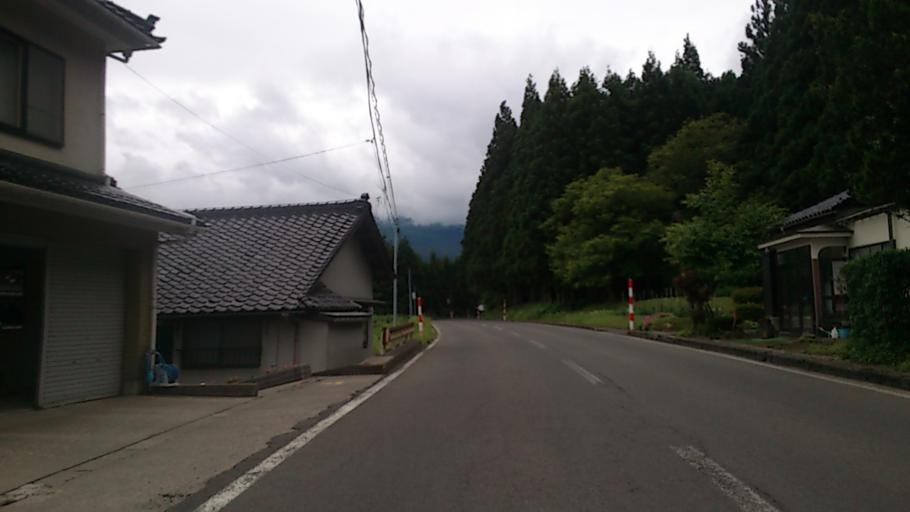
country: JP
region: Yamagata
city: Yuza
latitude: 39.1803
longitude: 139.9462
